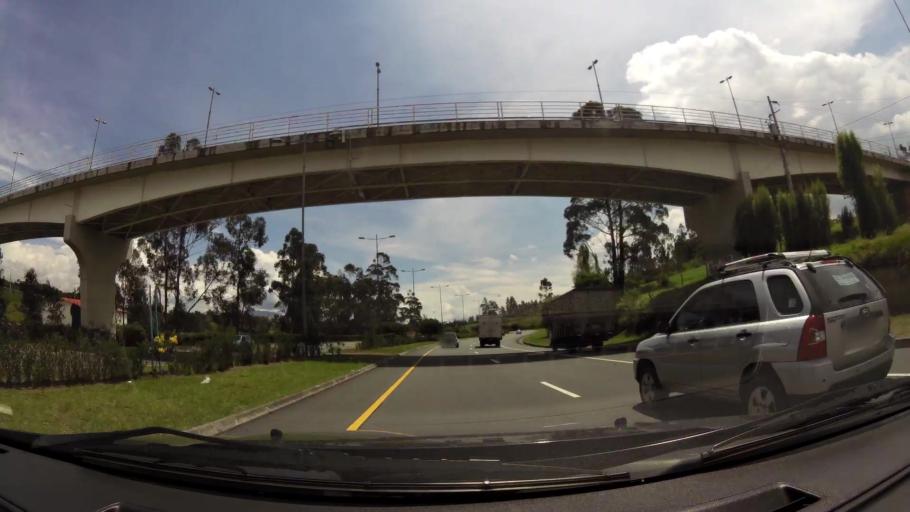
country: EC
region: Pichincha
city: Sangolqui
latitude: -0.1792
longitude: -78.3412
